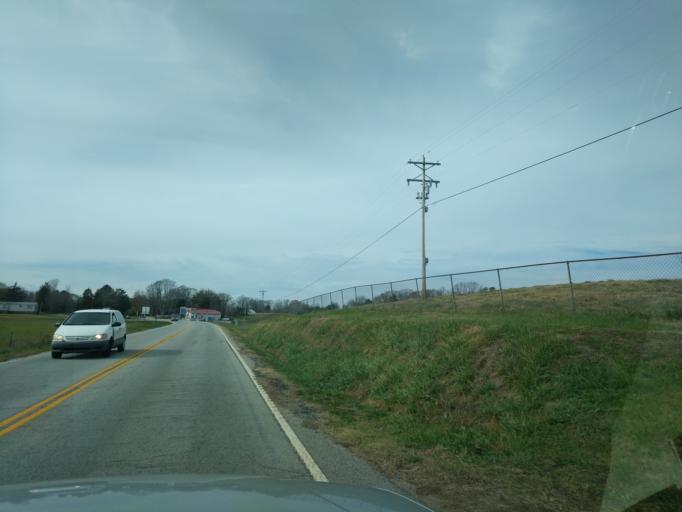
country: US
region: South Carolina
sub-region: Oconee County
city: Walhalla
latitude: 34.8052
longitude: -82.9751
